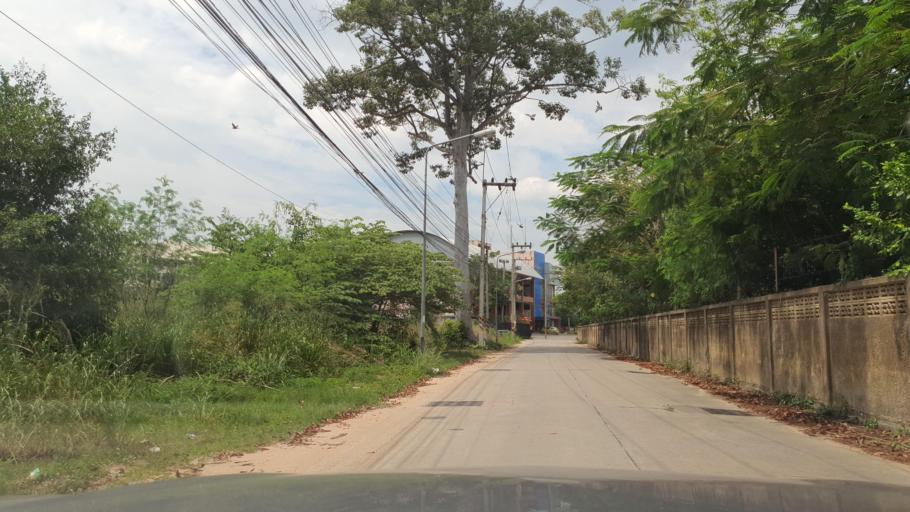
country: TH
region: Chon Buri
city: Phatthaya
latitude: 12.8882
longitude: 100.8930
